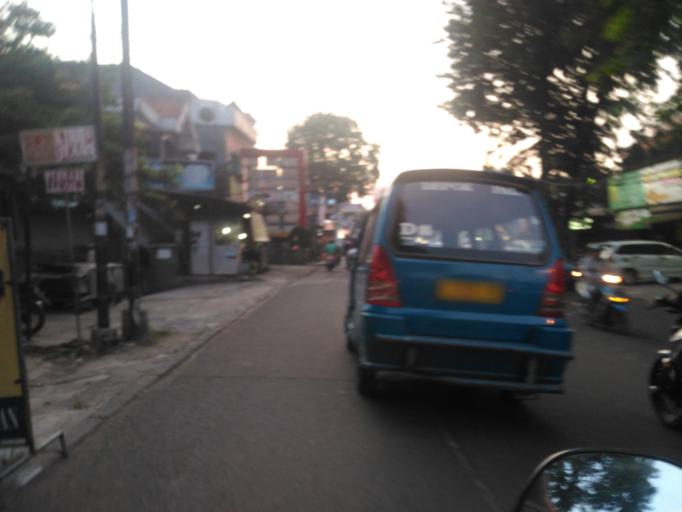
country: ID
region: West Java
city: Depok
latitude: -6.3549
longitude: 106.8402
